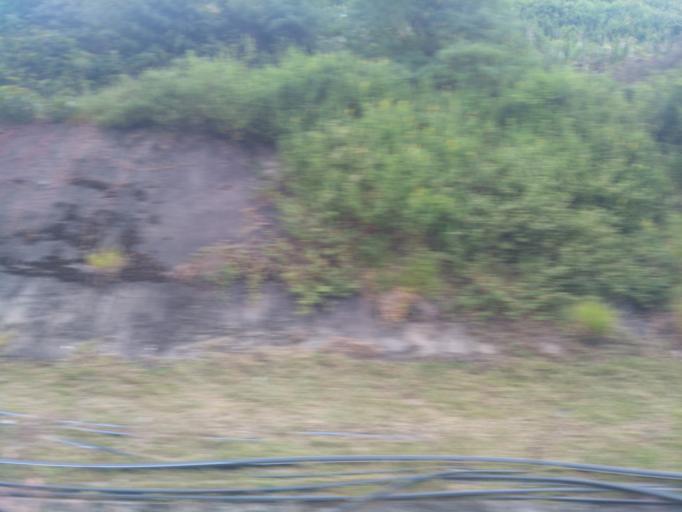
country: MY
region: Pahang
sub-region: Cameron Highlands
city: Tanah Rata
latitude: 4.5814
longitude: 101.4169
